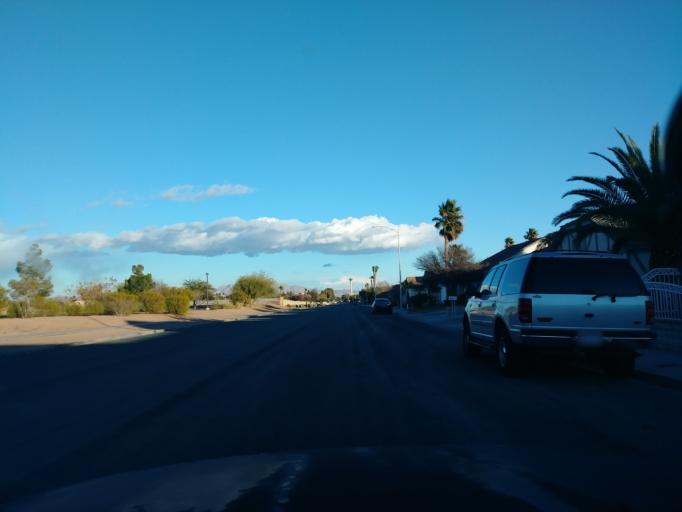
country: US
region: Nevada
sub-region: Clark County
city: Spring Valley
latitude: 36.1479
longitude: -115.2377
